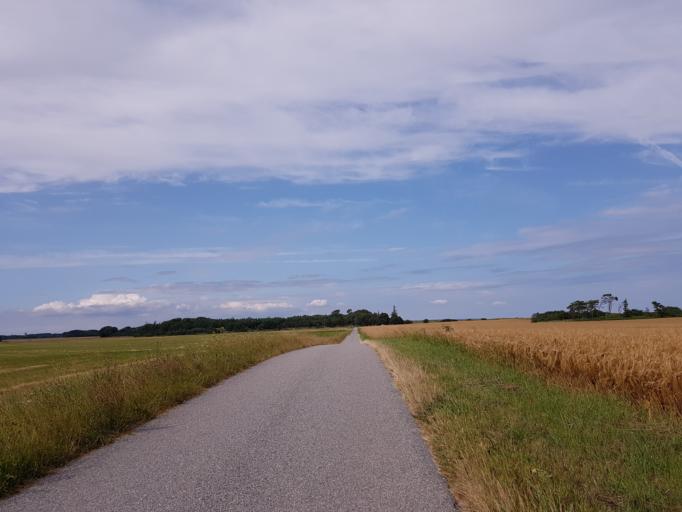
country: DK
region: Zealand
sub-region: Guldborgsund Kommune
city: Nykobing Falster
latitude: 54.5747
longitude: 11.9690
